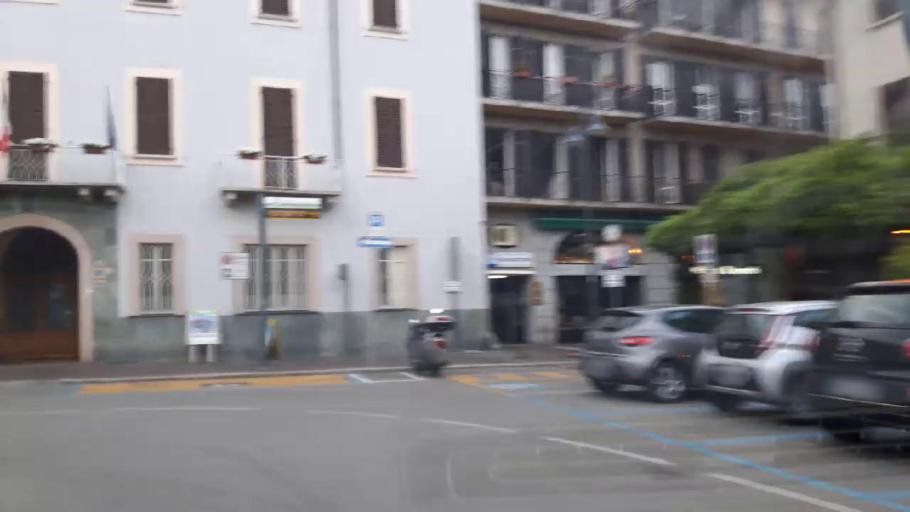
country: IT
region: Piedmont
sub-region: Provincia di Novara
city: Arona
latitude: 45.7600
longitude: 8.5617
